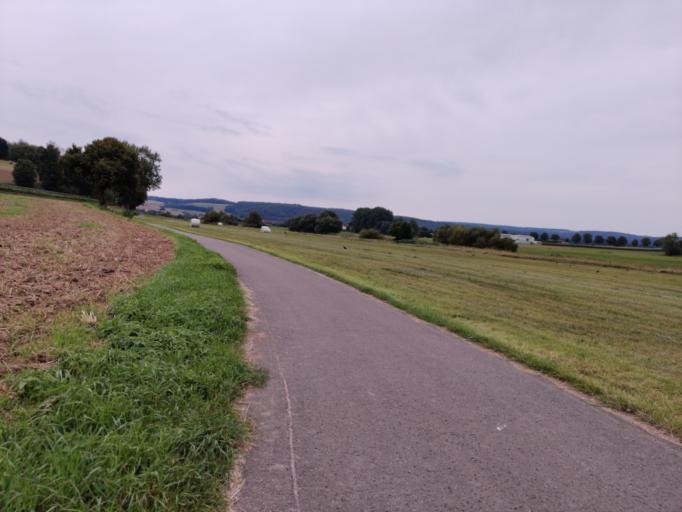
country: DE
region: Lower Saxony
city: Pegestorf
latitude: 51.9235
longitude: 9.4587
